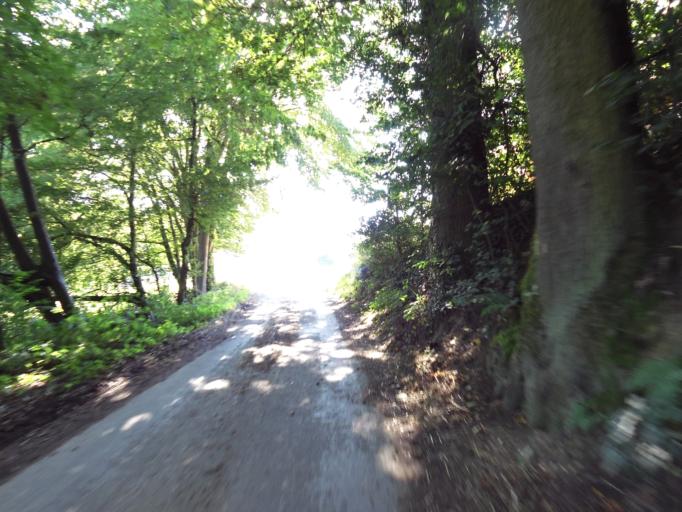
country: DE
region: Hesse
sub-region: Regierungsbezirk Darmstadt
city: Morlenbach
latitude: 49.5906
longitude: 8.7520
